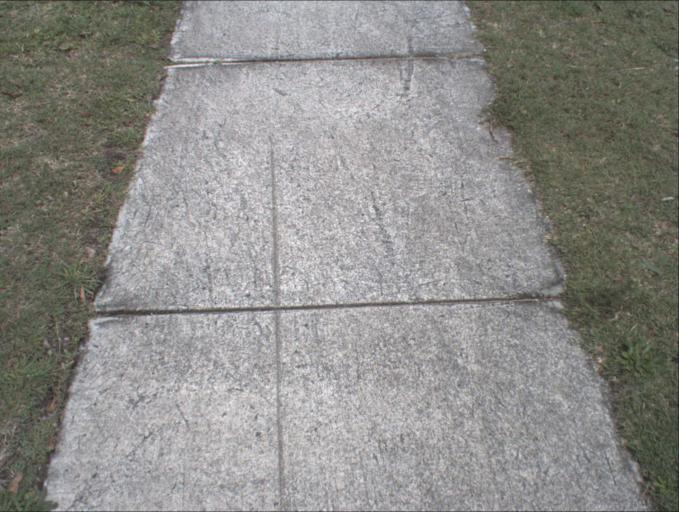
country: AU
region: Queensland
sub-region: Logan
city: Park Ridge South
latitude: -27.6719
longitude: 153.0279
